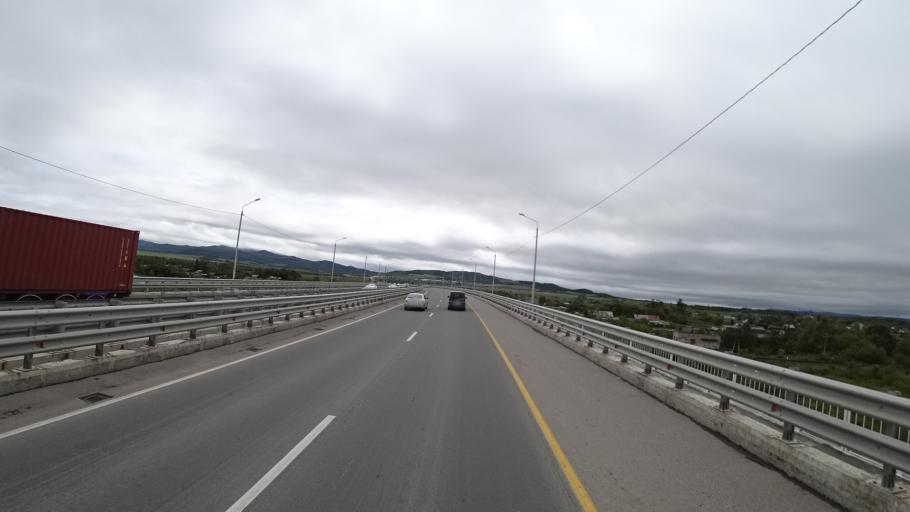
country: RU
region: Primorskiy
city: Monastyrishche
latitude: 44.1932
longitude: 132.4426
